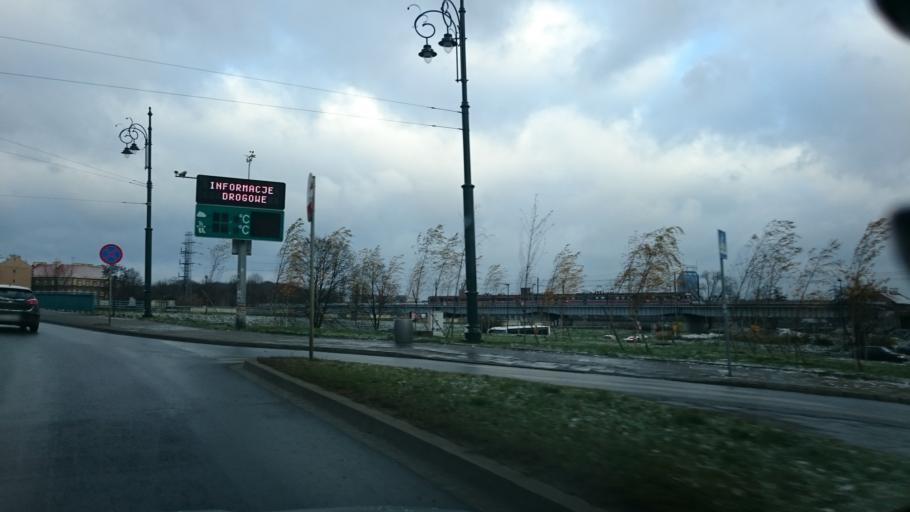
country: PL
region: Lesser Poland Voivodeship
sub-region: Krakow
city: Krakow
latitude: 50.0482
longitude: 19.9546
